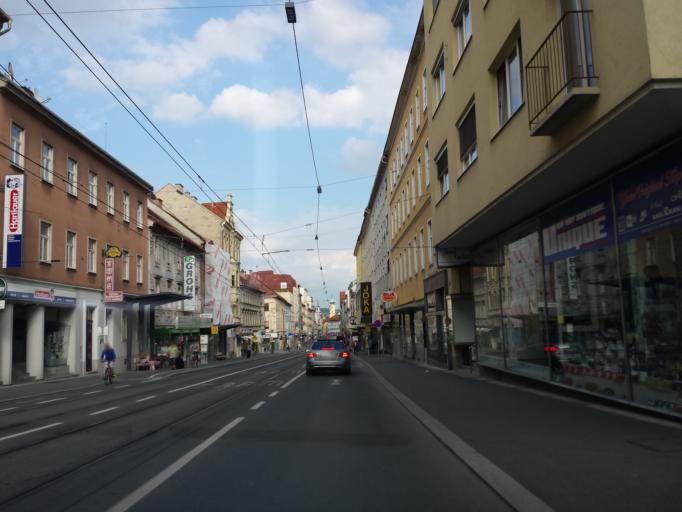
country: AT
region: Styria
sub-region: Graz Stadt
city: Graz
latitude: 47.0713
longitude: 15.4228
